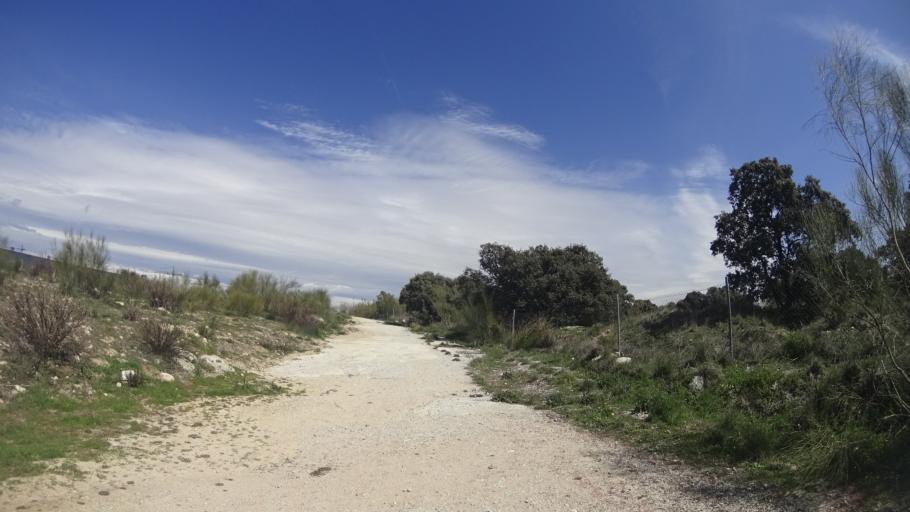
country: ES
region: Madrid
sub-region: Provincia de Madrid
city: Torrelodones
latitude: 40.5623
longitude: -3.9157
